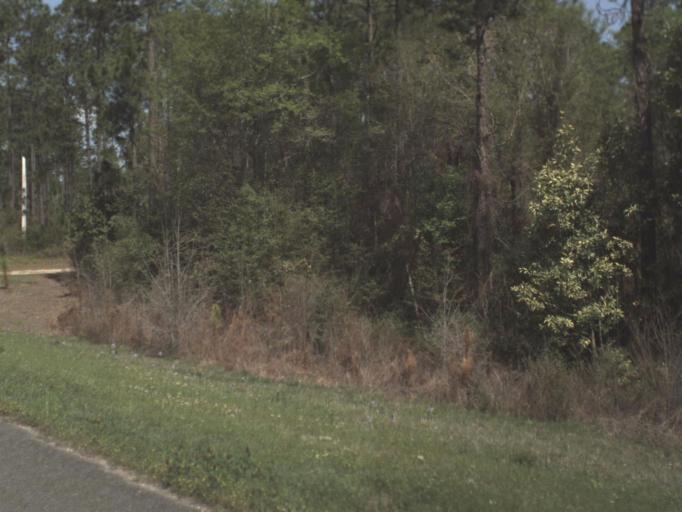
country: US
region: Florida
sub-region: Santa Rosa County
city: Point Baker
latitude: 30.8884
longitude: -86.9719
